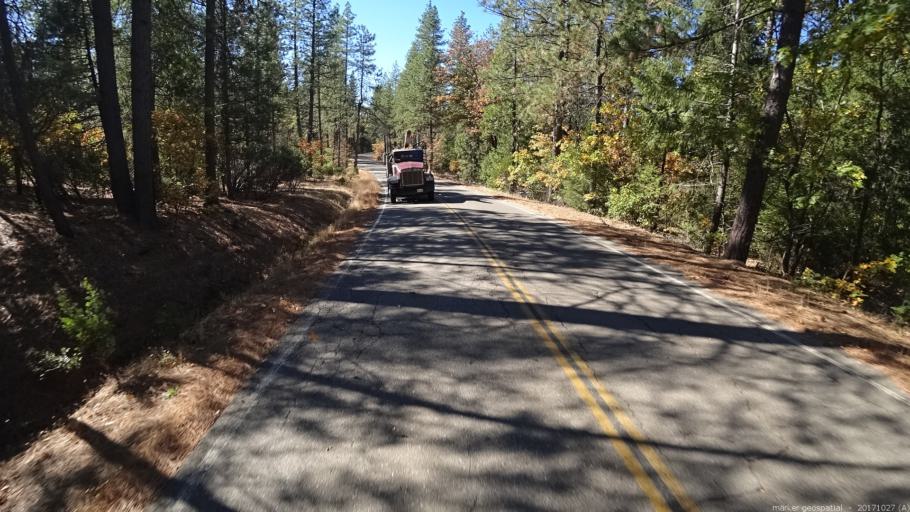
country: US
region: California
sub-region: Shasta County
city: Shingletown
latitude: 40.7119
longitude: -121.9529
